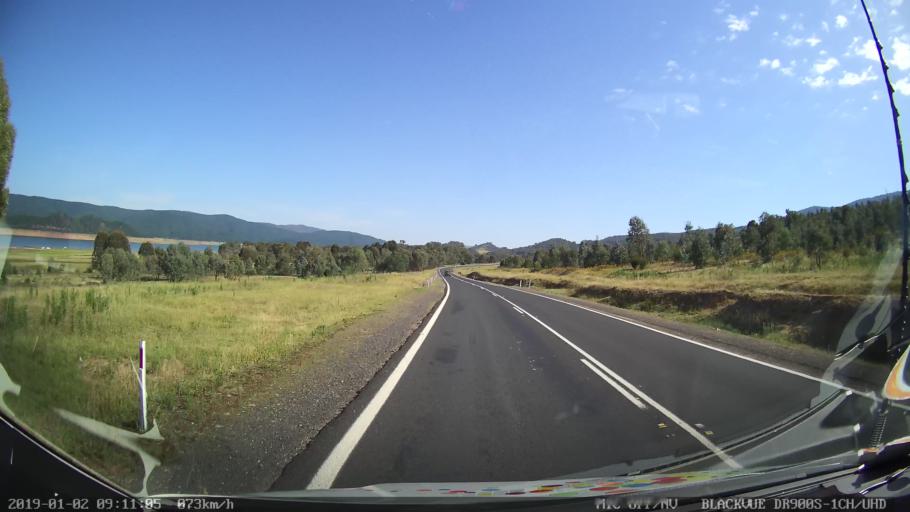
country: AU
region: New South Wales
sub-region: Tumut Shire
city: Tumut
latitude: -35.5150
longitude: 148.2688
